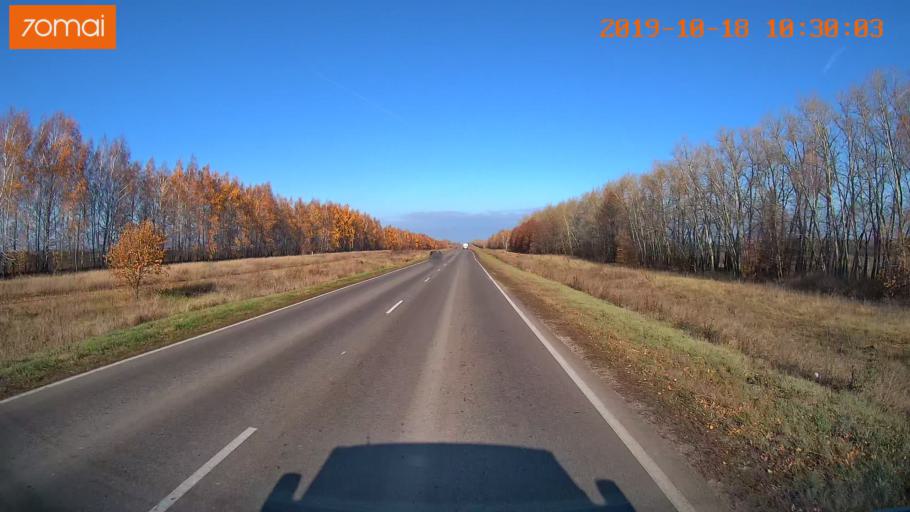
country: RU
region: Tula
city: Kurkino
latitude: 53.4599
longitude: 38.6488
